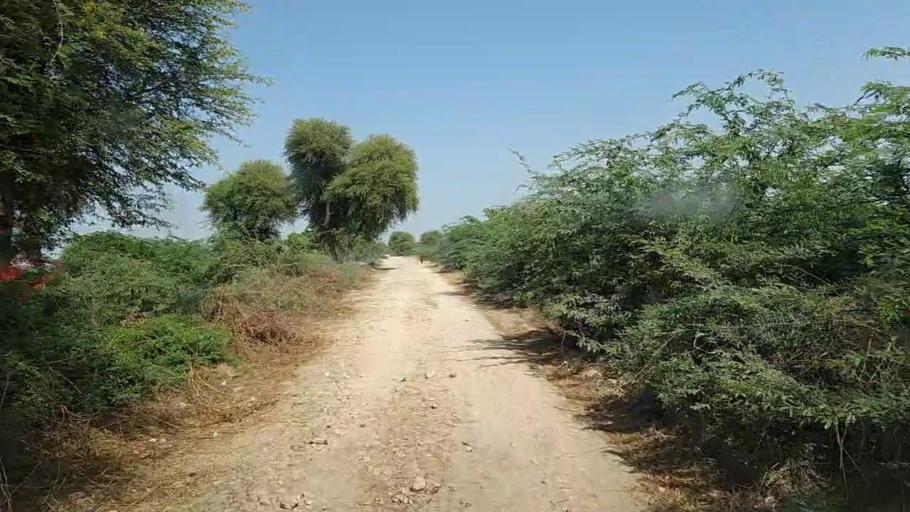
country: PK
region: Sindh
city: Mirpur Batoro
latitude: 24.7138
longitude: 68.4355
